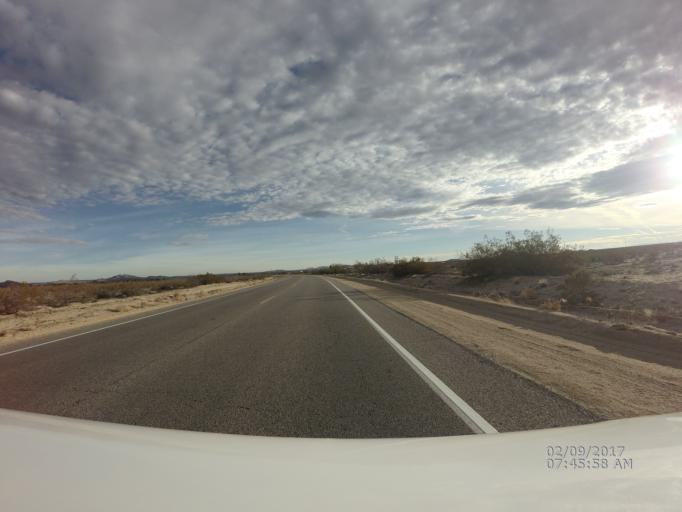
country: US
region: California
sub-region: Los Angeles County
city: Lake Los Angeles
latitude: 34.5493
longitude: -117.8303
